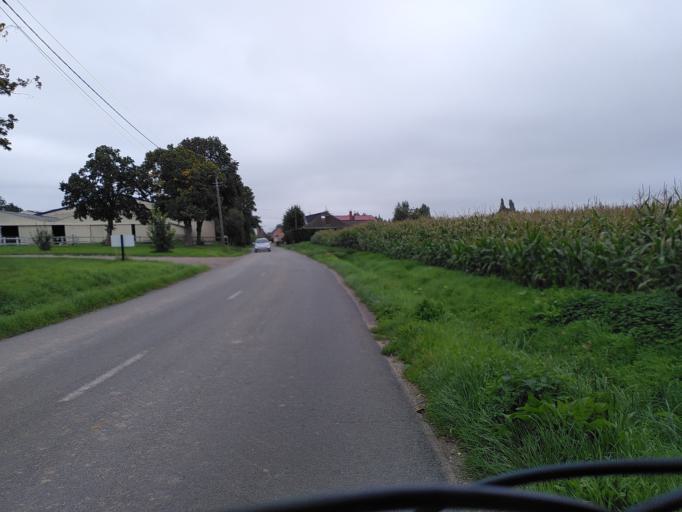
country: FR
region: Nord-Pas-de-Calais
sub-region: Departement du Pas-de-Calais
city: Aire-sur-la-Lys
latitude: 50.6474
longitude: 2.3863
